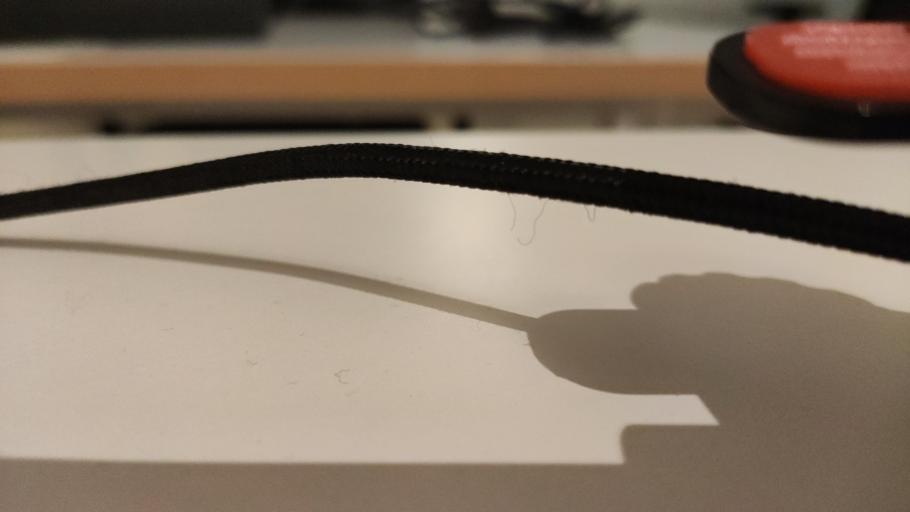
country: RU
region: Moskovskaya
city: Il'inskiy Pogost
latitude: 55.5303
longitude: 38.8724
